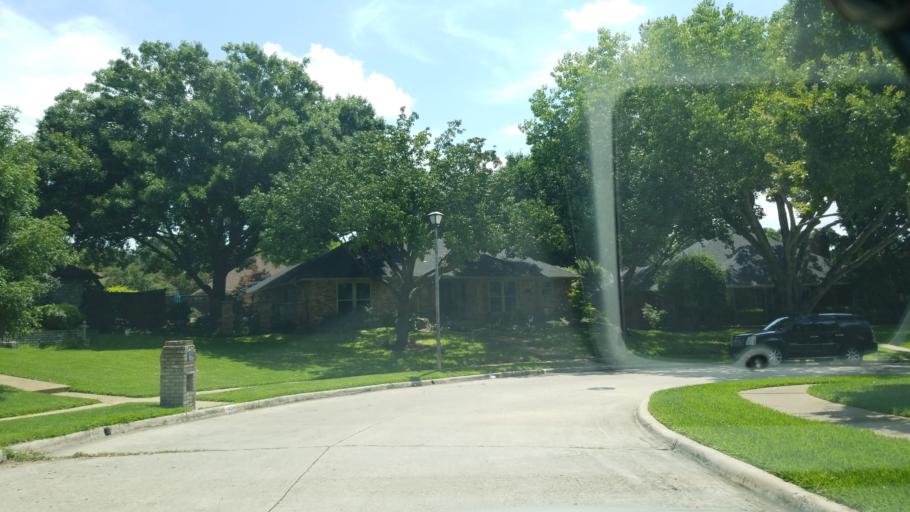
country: US
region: Texas
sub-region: Dallas County
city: Coppell
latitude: 32.9641
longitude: -96.9749
